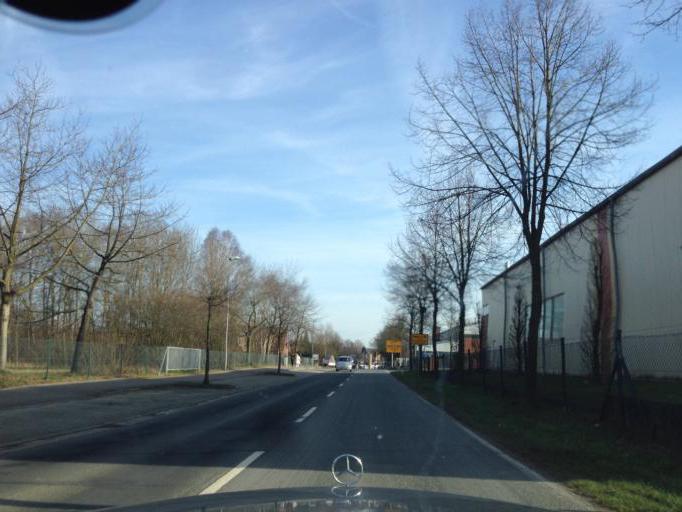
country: DE
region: Lower Saxony
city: Hasbergen
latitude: 52.2100
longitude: 7.9163
